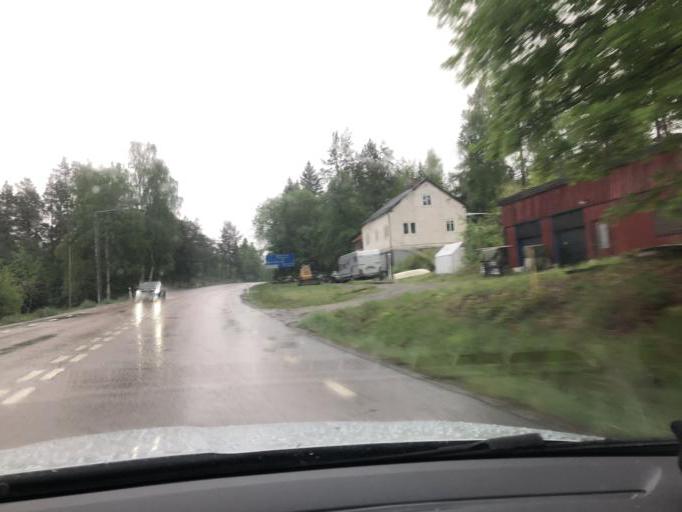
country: SE
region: Vaesternorrland
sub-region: Haernoesands Kommun
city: Haernoesand
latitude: 62.7898
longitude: 17.9160
